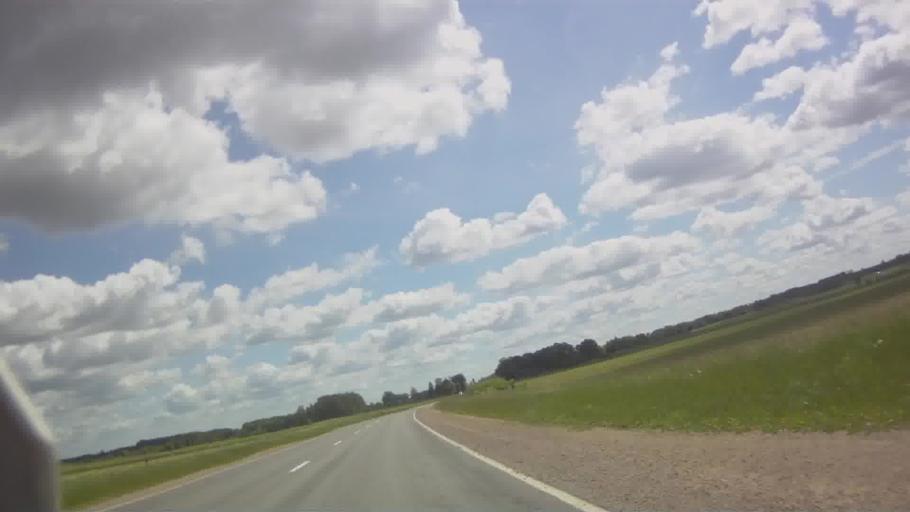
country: LV
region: Vilanu
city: Vilani
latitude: 56.5997
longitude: 26.8678
